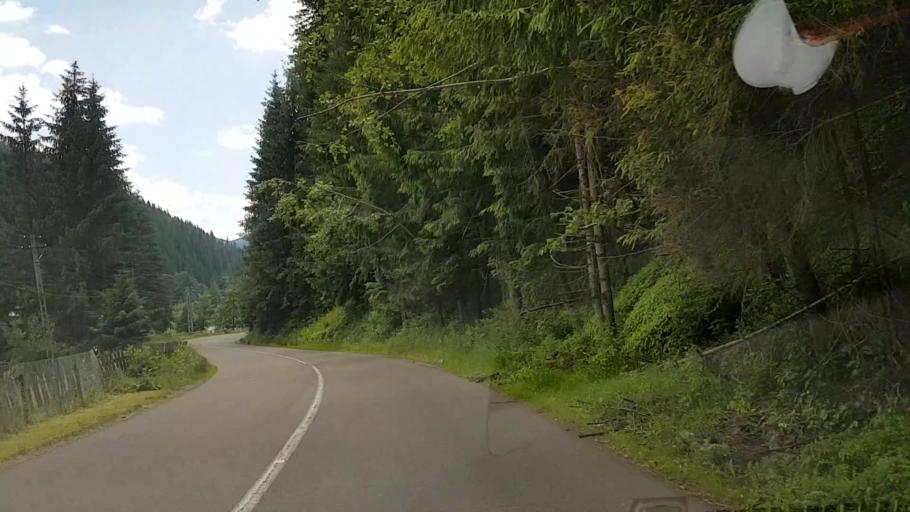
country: RO
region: Suceava
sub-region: Comuna Crucea
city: Crucea
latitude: 47.3472
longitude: 25.6064
